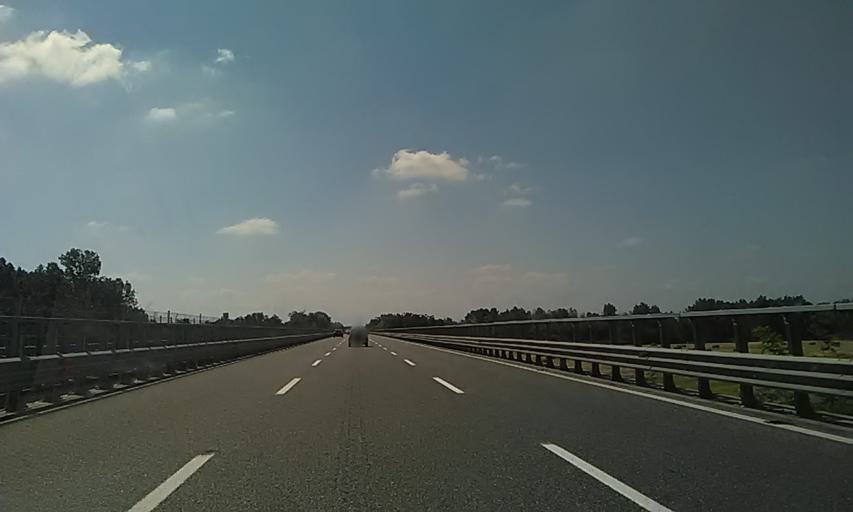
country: IT
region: Piedmont
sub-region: Provincia di Alessandria
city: Castellazzo Bormida
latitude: 44.8629
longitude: 8.5814
